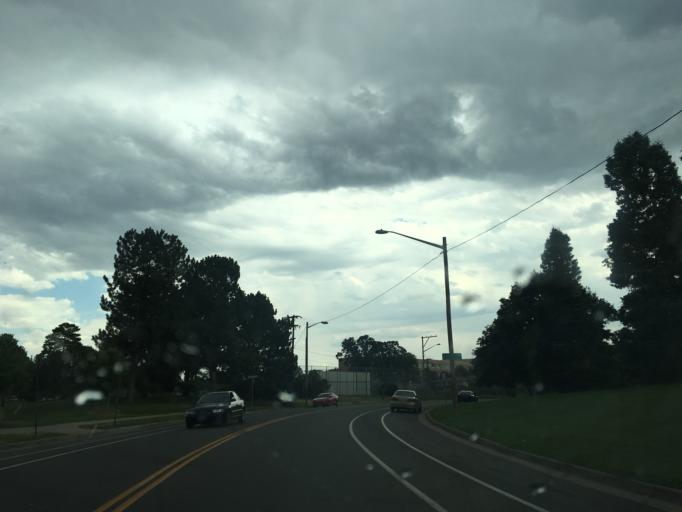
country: US
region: Colorado
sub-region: Arapahoe County
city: Sheridan
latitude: 39.6781
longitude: -105.0426
